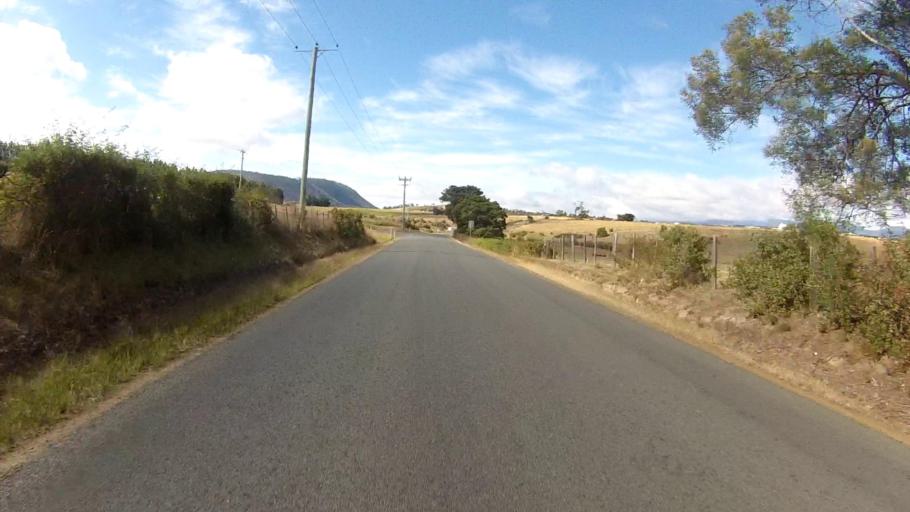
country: AU
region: Tasmania
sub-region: Brighton
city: Old Beach
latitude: -42.7556
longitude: 147.2797
